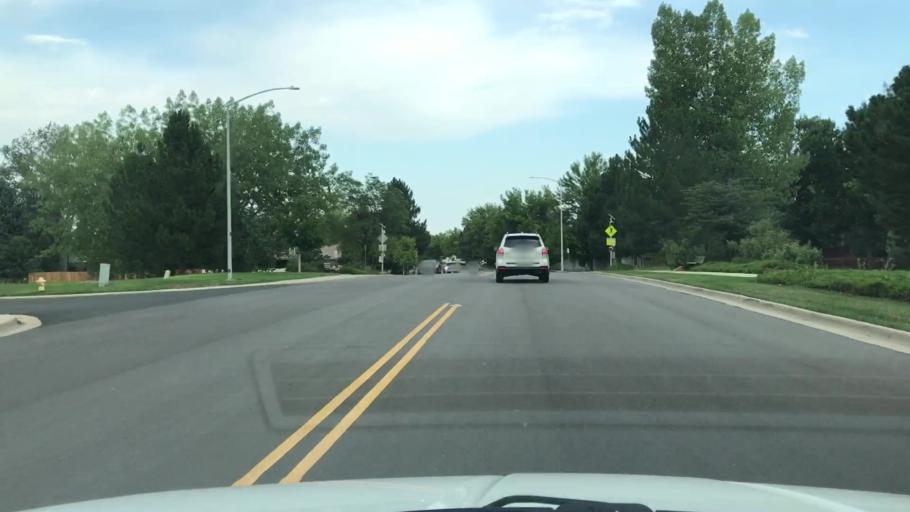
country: US
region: Colorado
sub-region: Broomfield County
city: Broomfield
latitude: 39.9335
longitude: -105.0828
